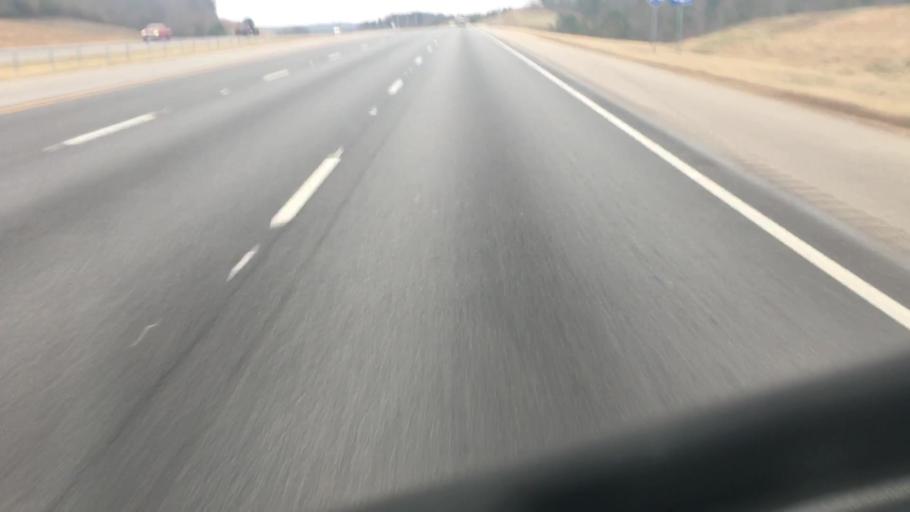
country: US
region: Alabama
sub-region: Jefferson County
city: Fultondale
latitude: 33.5825
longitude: -86.8277
